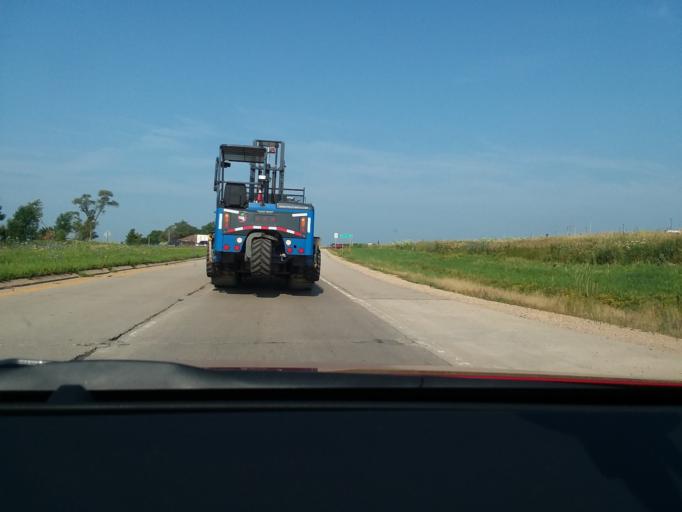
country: US
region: Wisconsin
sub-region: Dane County
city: Windsor
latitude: 43.1946
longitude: -89.3473
